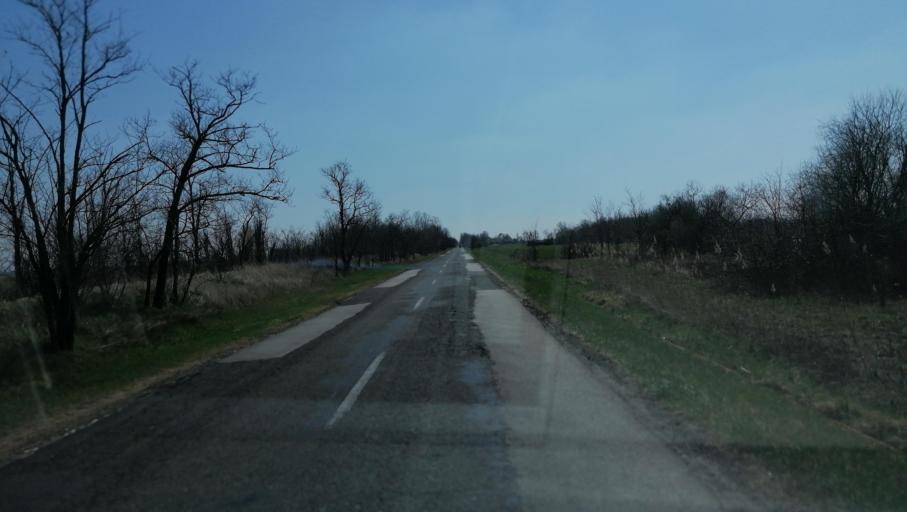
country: HU
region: Pest
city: Domsod
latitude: 47.1060
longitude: 19.0909
